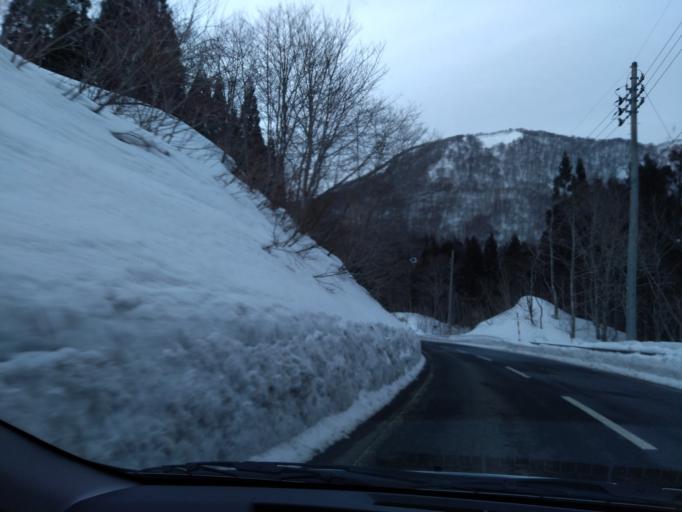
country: JP
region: Iwate
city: Kitakami
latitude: 39.2362
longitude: 140.9159
